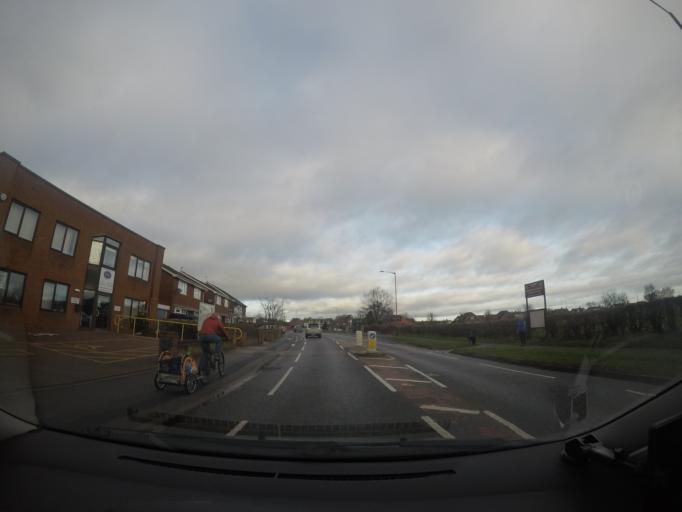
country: GB
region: England
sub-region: City of York
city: Huntington
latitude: 53.9973
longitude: -1.0573
